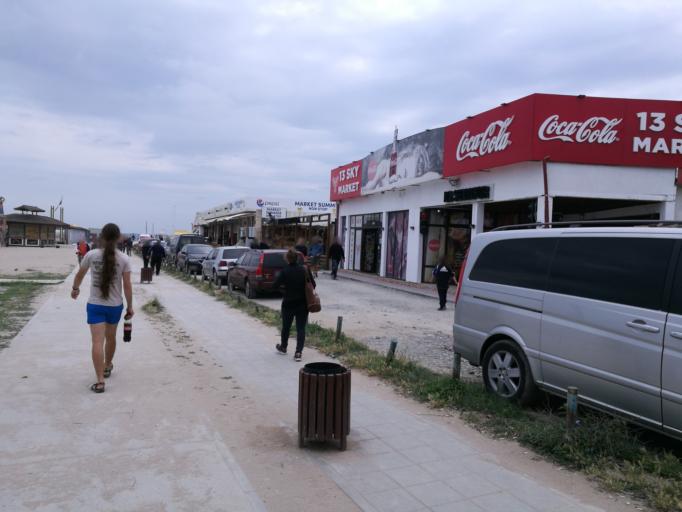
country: RO
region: Constanta
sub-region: Municipiul Mangalia
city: Mangalia
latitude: 43.7508
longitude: 28.5765
